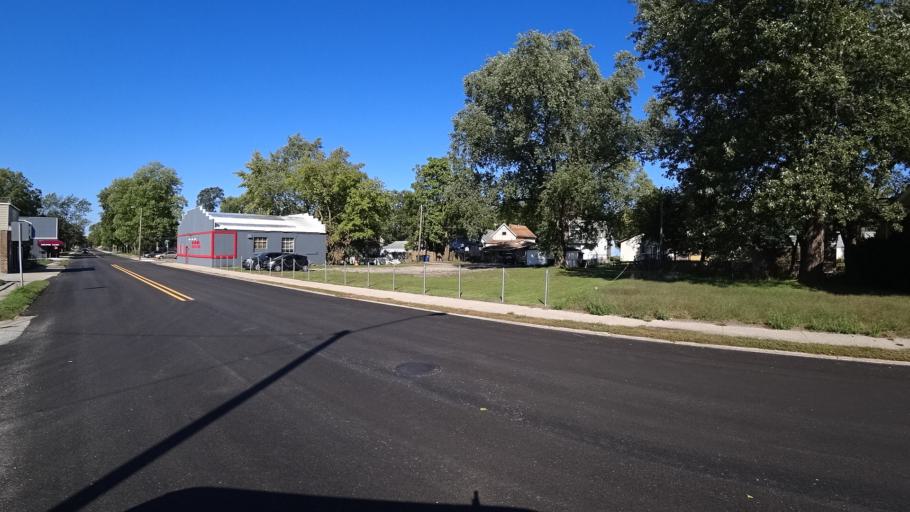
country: US
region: Indiana
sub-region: LaPorte County
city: Michigan City
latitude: 41.7060
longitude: -86.8886
